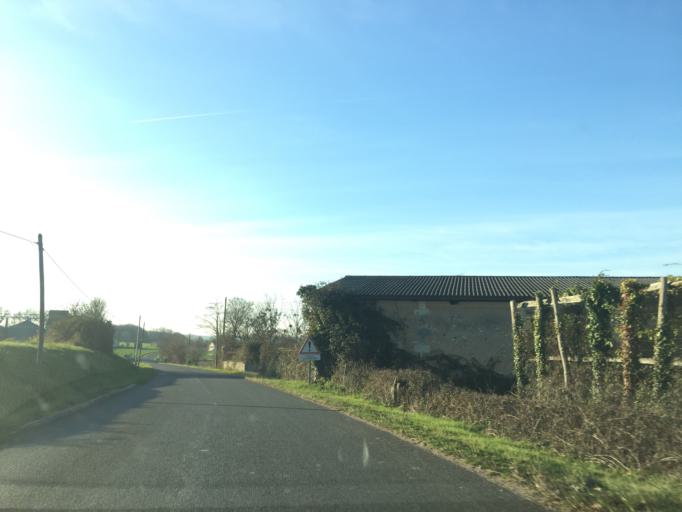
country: FR
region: Aquitaine
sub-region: Departement de la Dordogne
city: Saint-Aulaye
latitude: 45.2534
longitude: 0.2076
